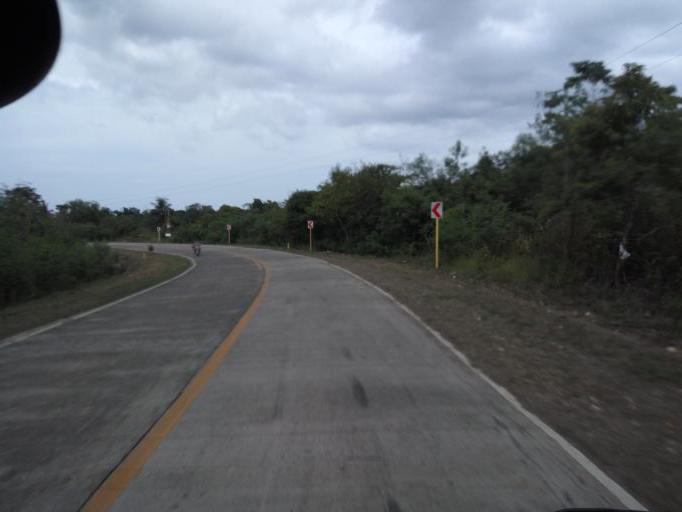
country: PH
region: Cagayan Valley
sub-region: Province of Cagayan
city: Magapit, Aguiguican
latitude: 18.1296
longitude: 121.7082
